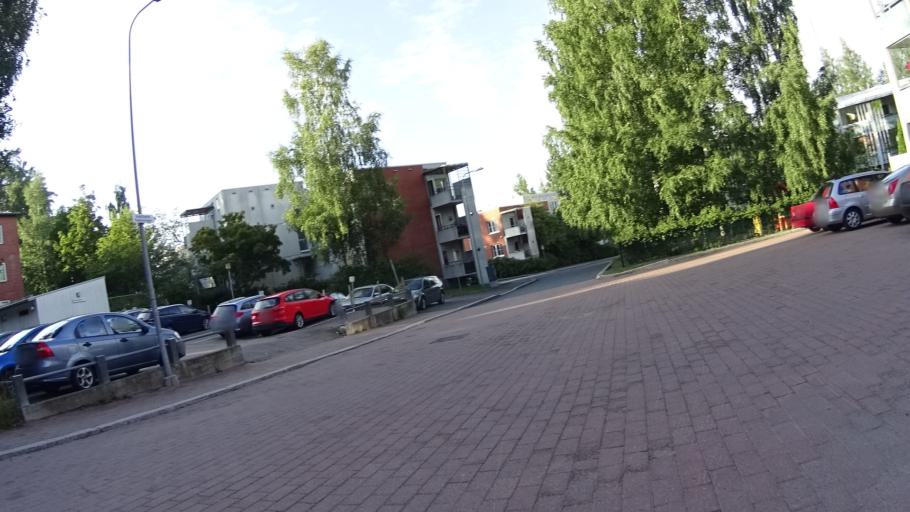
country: FI
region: Uusimaa
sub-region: Helsinki
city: Teekkarikylae
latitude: 60.2515
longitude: 24.8654
